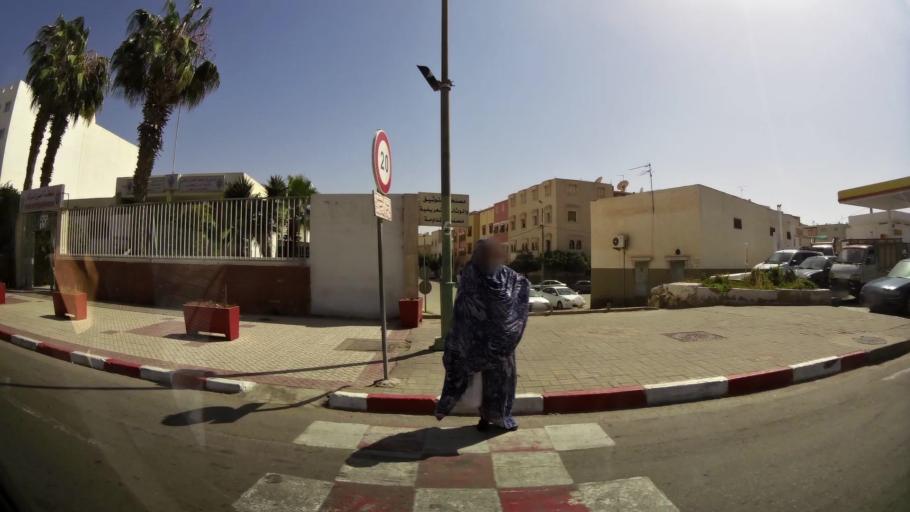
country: MA
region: Souss-Massa-Draa
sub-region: Inezgane-Ait Mellou
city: Inezgane
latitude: 30.3628
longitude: -9.5346
